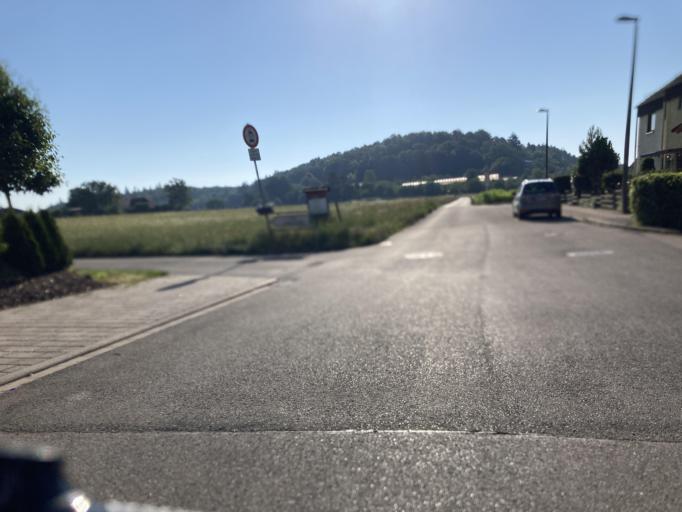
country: DE
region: Baden-Wuerttemberg
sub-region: Regierungsbezirk Stuttgart
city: Renningen
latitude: 48.7766
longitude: 8.9440
